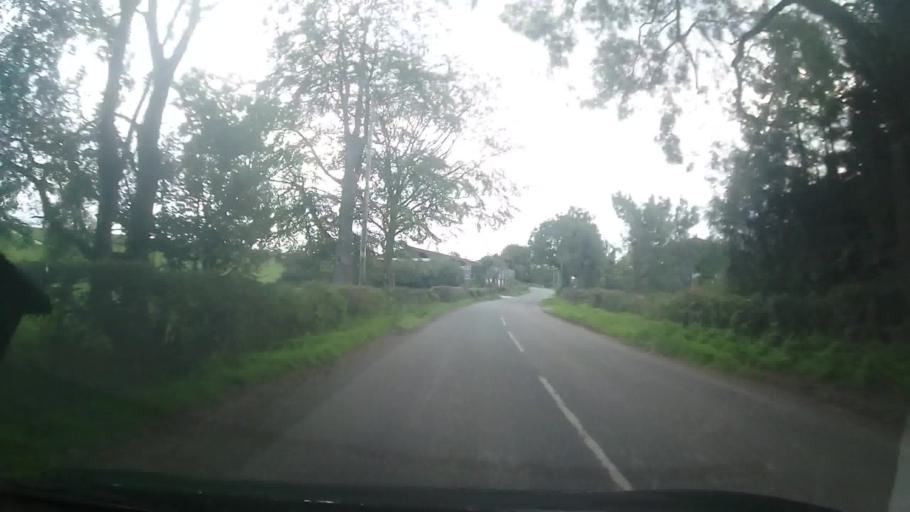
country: GB
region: England
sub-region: Shropshire
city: Bishop's Castle
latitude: 52.4820
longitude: -2.9894
